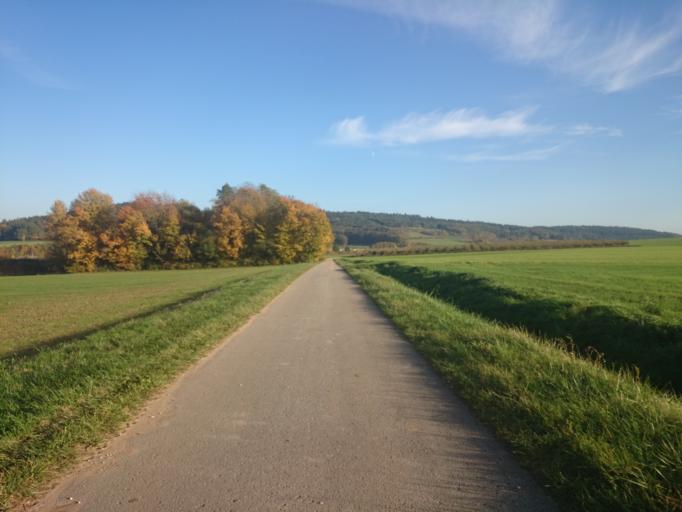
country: DE
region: Bavaria
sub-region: Regierungsbezirk Mittelfranken
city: Thalmassing
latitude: 49.1333
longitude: 11.2616
